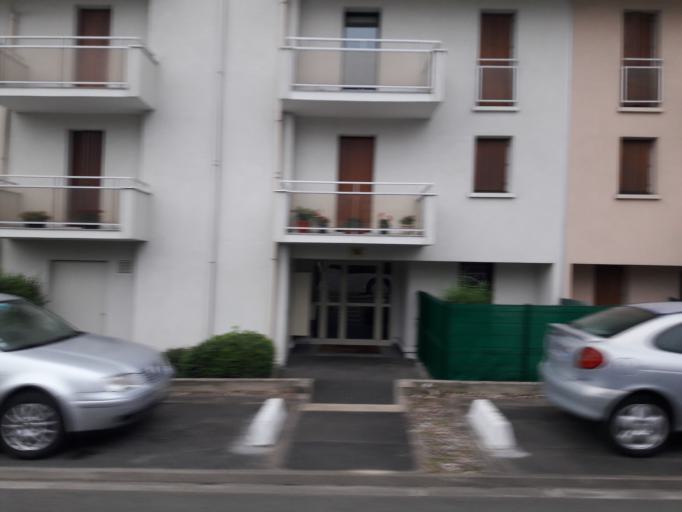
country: FR
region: Ile-de-France
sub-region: Departement de l'Essonne
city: Longjumeau
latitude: 48.6992
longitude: 2.2987
